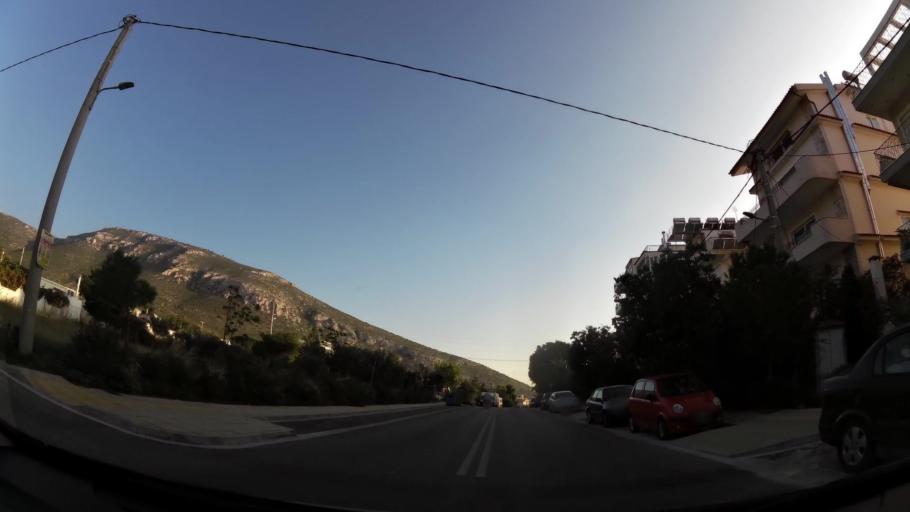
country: GR
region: Attica
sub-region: Nomarchia Athinas
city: Argyroupoli
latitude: 37.8913
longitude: 23.7769
